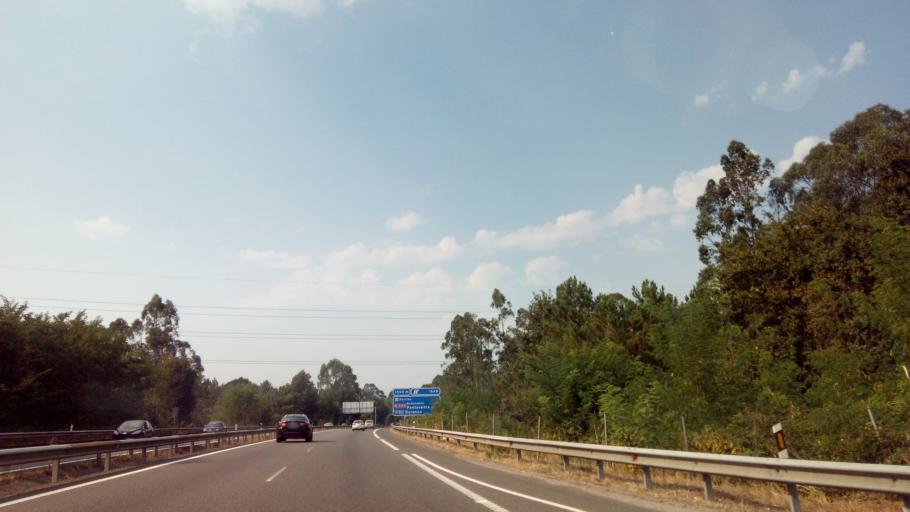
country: ES
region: Galicia
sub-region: Provincia de Pontevedra
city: Porrino
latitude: 42.1526
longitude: -8.6259
